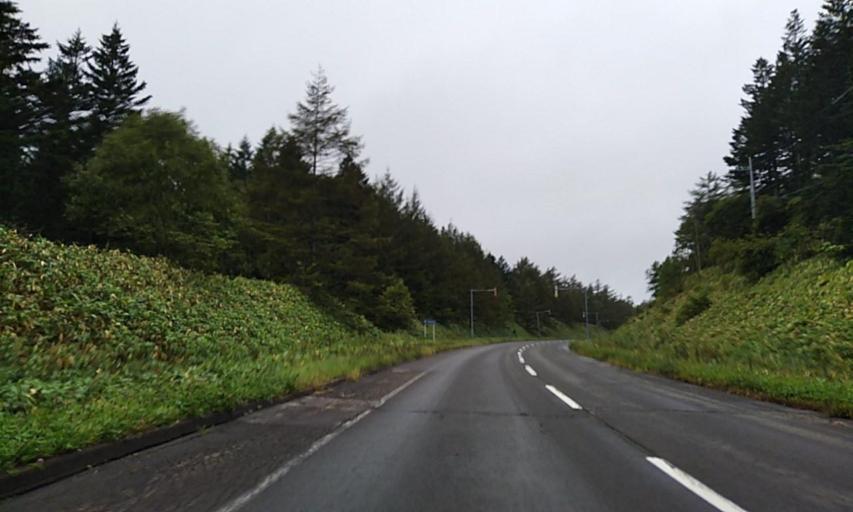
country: JP
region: Hokkaido
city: Kushiro
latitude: 43.4776
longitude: 144.5620
